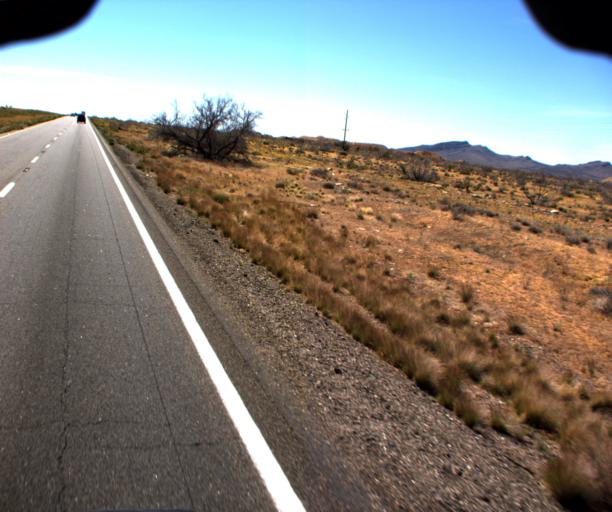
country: US
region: Arizona
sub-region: Mohave County
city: Dolan Springs
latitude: 35.4273
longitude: -114.2816
